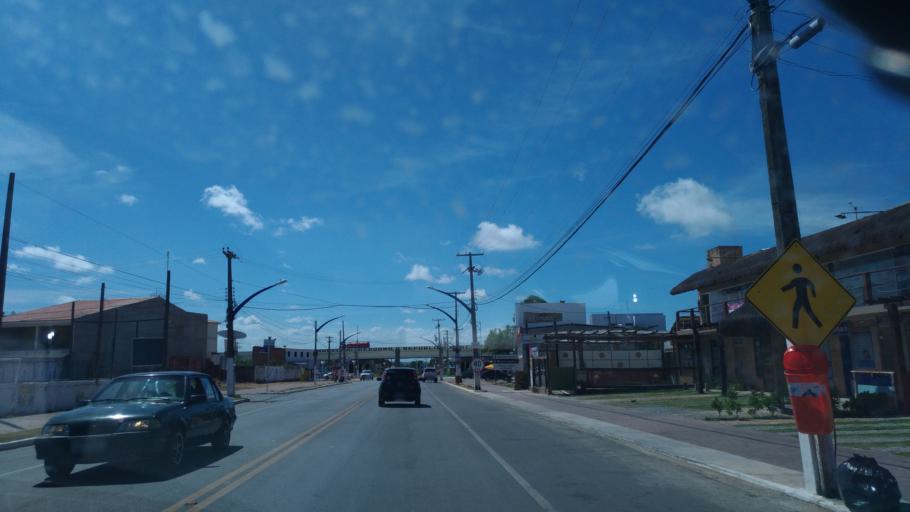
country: BR
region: Alagoas
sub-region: Marechal Deodoro
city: Marechal Deodoro
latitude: -9.7678
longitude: -35.8492
